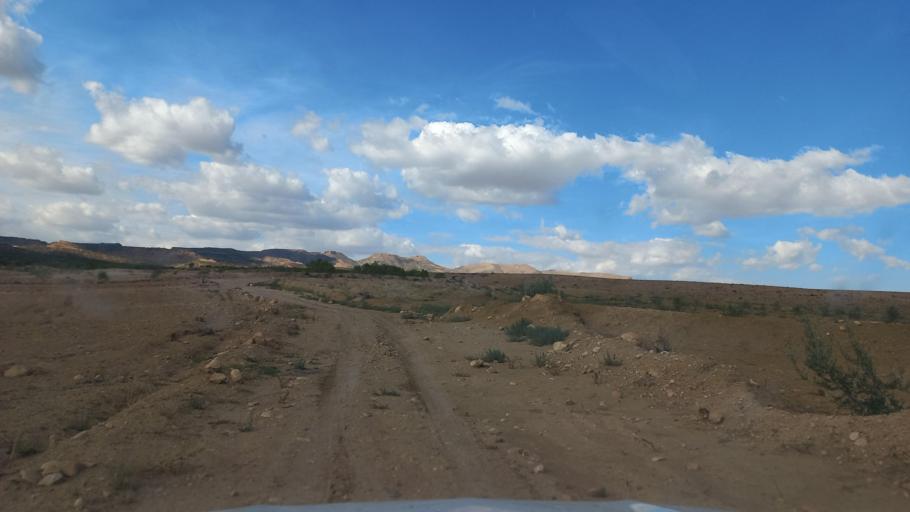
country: TN
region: Al Qasrayn
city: Sbiba
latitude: 35.4015
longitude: 9.0114
